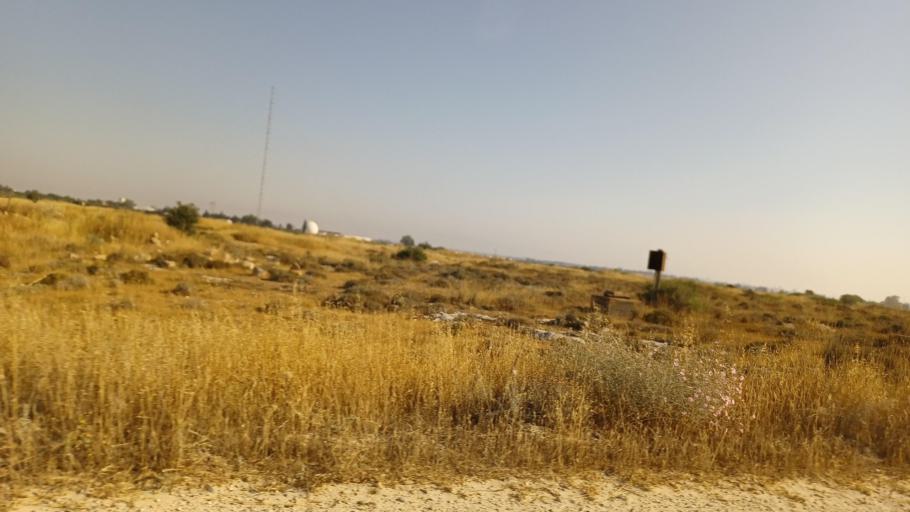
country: CY
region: Ammochostos
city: Frenaros
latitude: 35.0752
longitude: 33.9009
